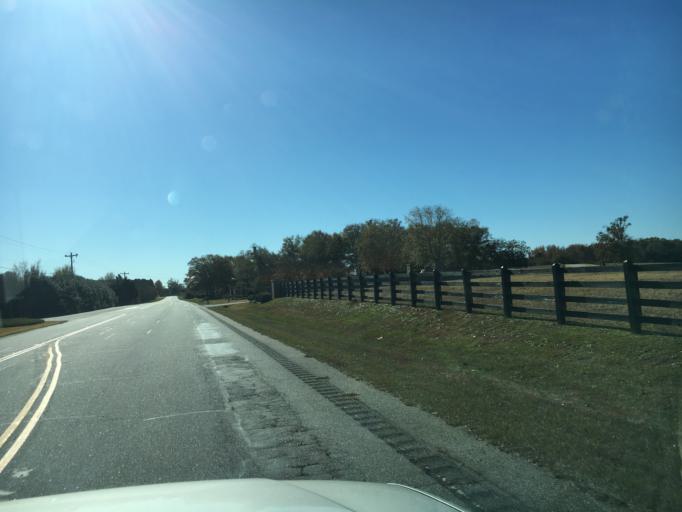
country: US
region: South Carolina
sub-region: Anderson County
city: Centerville
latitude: 34.4843
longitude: -82.7842
